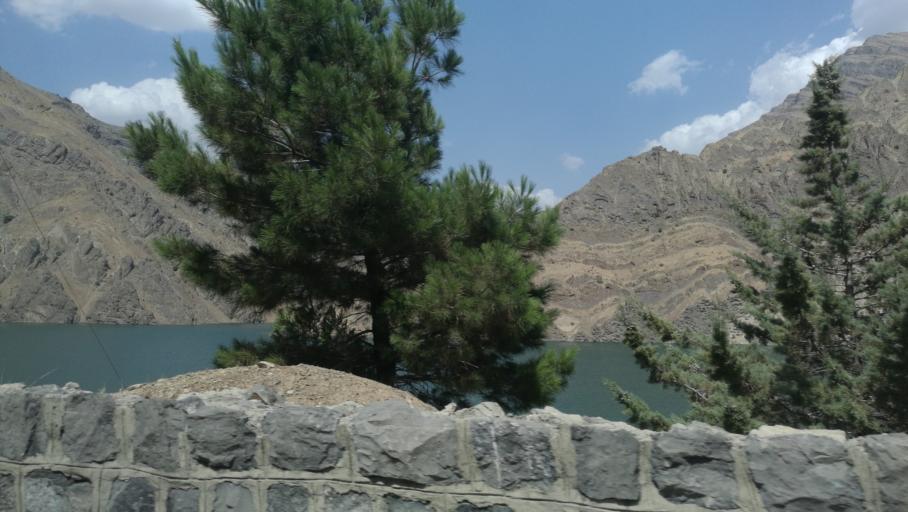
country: IR
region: Alborz
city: Karaj
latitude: 35.9756
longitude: 51.0972
